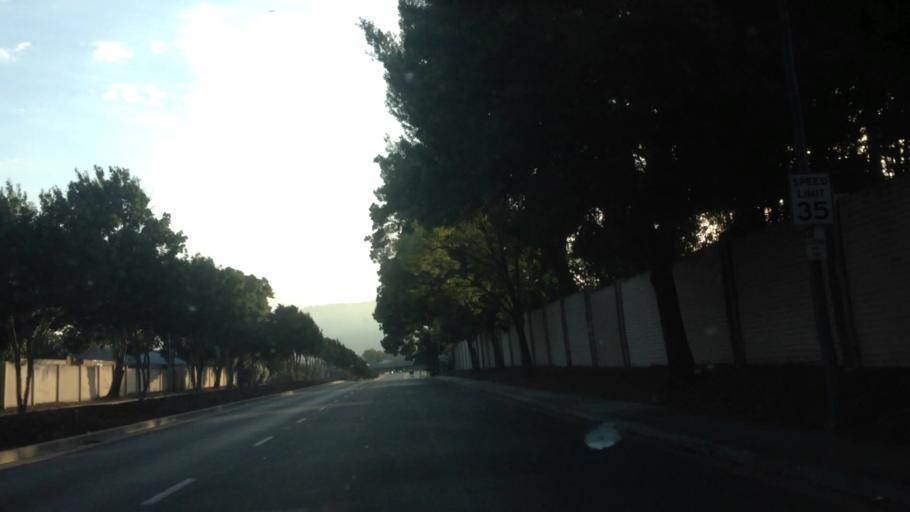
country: US
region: California
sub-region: Santa Clara County
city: Seven Trees
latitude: 37.2923
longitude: -121.8133
